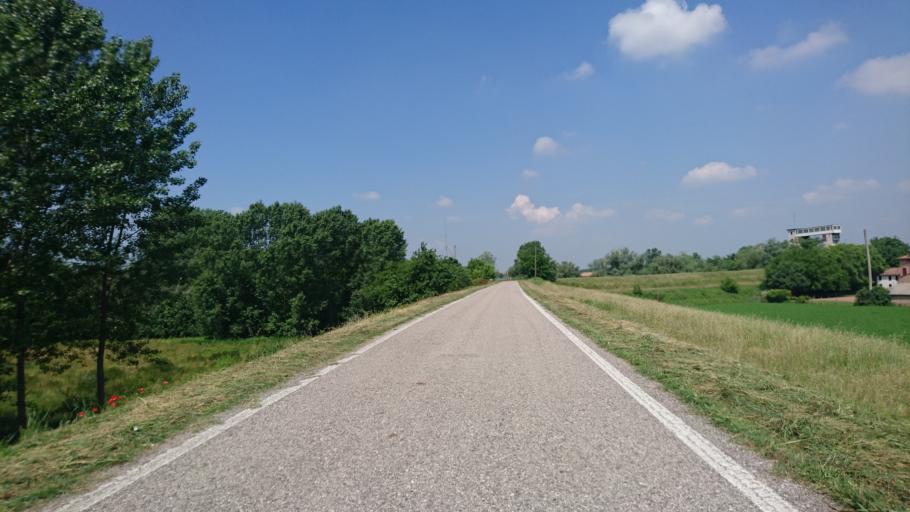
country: IT
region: Lombardy
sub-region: Provincia di Mantova
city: Sustinente
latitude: 45.0749
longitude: 10.9797
